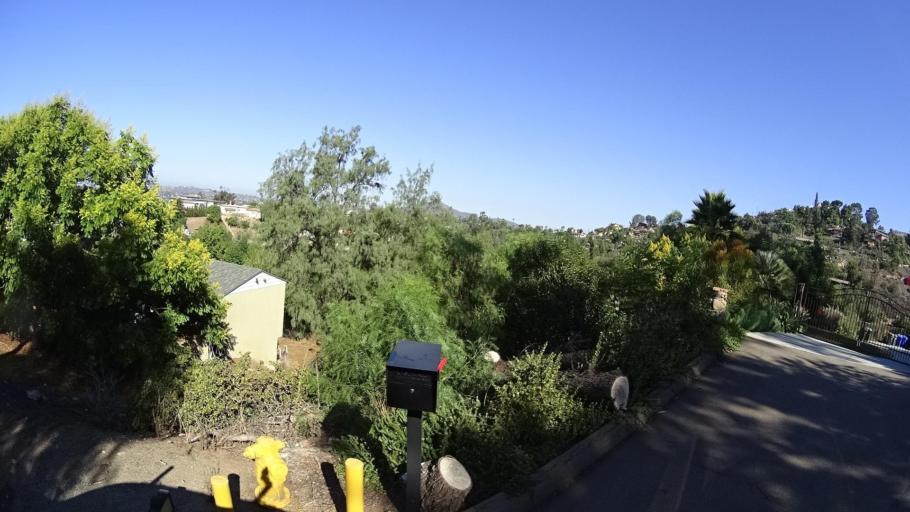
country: US
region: California
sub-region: San Diego County
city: Casa de Oro-Mount Helix
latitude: 32.7691
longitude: -116.9921
